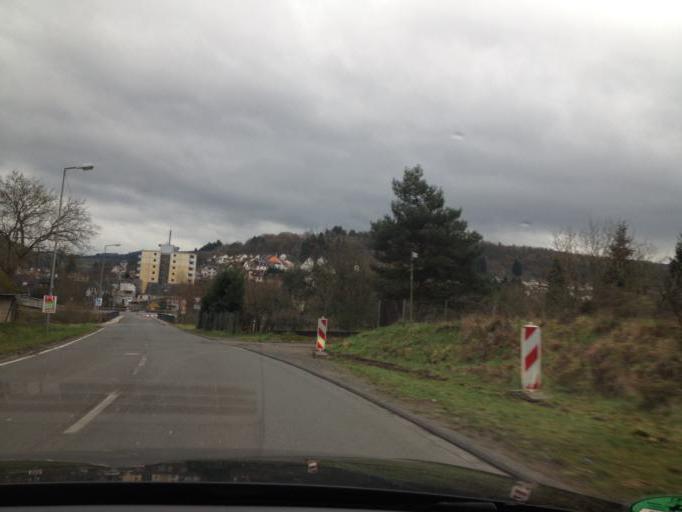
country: DE
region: Rheinland-Pfalz
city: Hintertiefenbach
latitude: 49.7160
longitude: 7.3650
